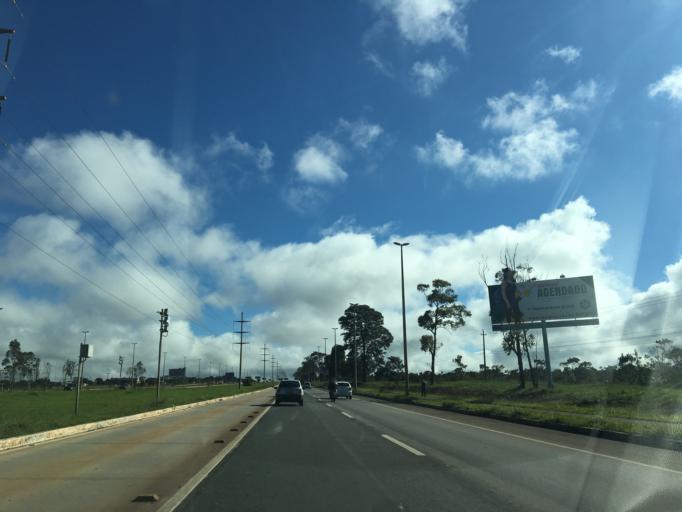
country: BR
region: Federal District
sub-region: Brasilia
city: Brasilia
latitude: -15.9851
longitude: -48.0417
